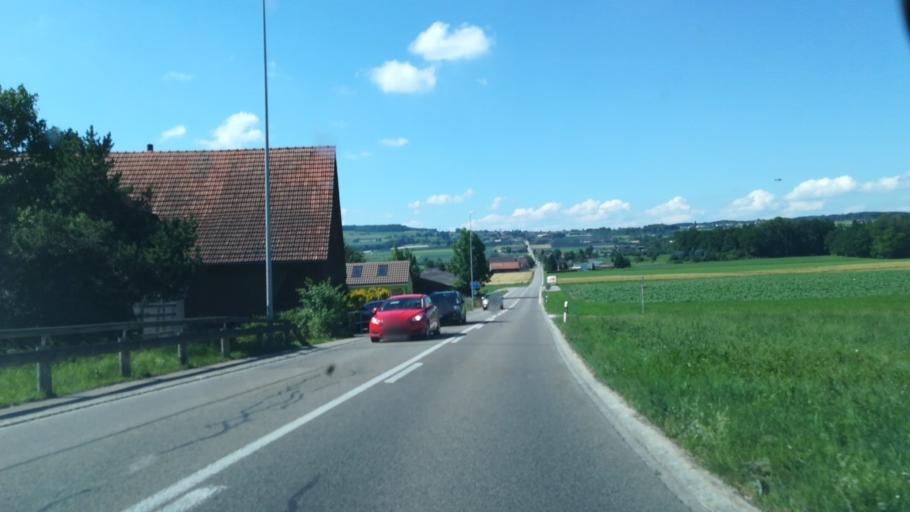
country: CH
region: Thurgau
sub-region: Weinfelden District
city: Sulgen
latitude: 47.5493
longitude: 9.1776
